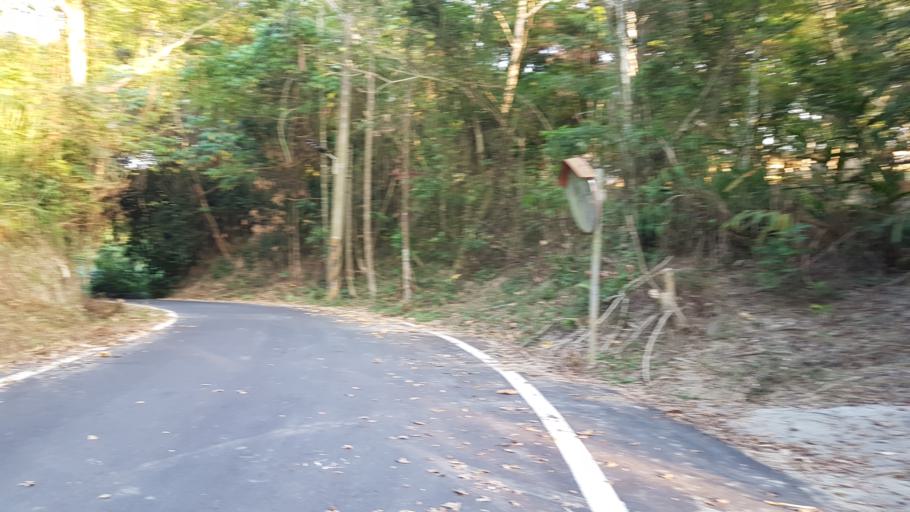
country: TW
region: Taiwan
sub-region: Chiayi
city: Jiayi Shi
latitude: 23.3622
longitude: 120.4660
